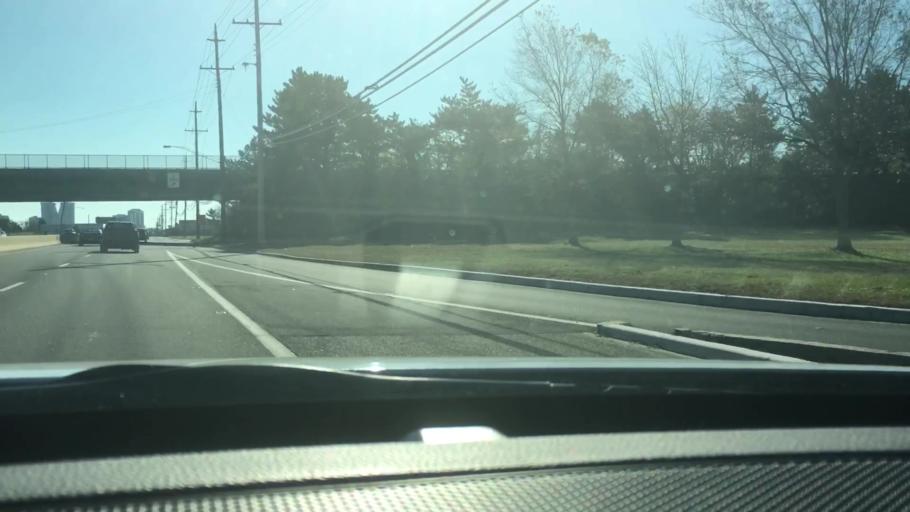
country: US
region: New Jersey
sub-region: Atlantic County
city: Ventnor City
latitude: 39.3683
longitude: -74.4742
